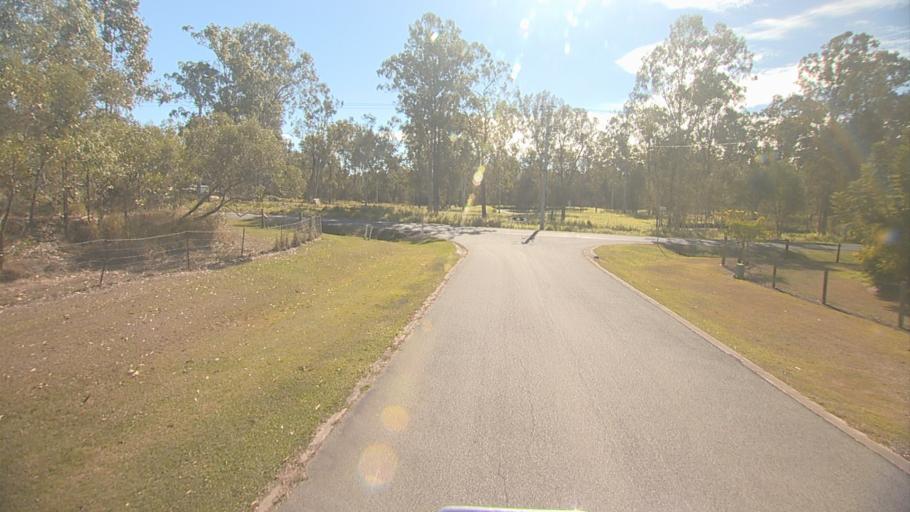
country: AU
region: Queensland
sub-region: Logan
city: North Maclean
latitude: -27.7988
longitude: 153.0444
